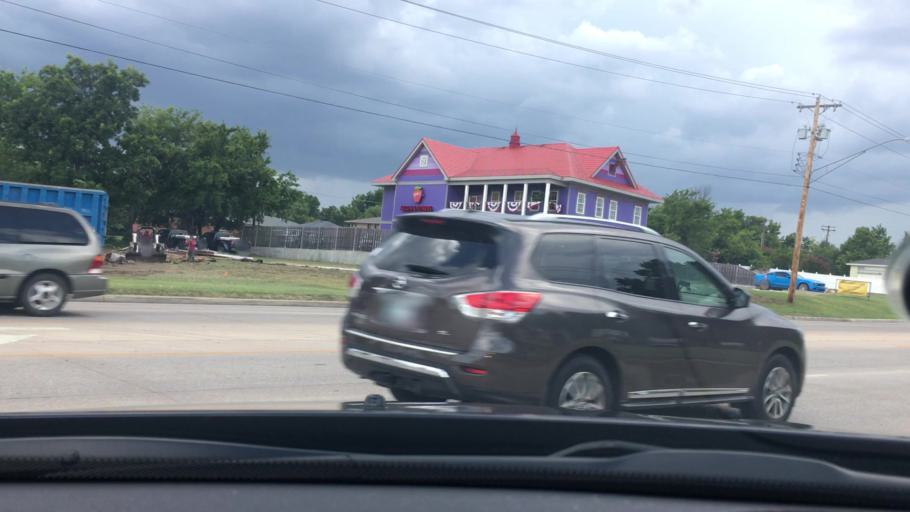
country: US
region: Oklahoma
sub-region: Pontotoc County
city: Ada
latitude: 34.7818
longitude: -96.6574
